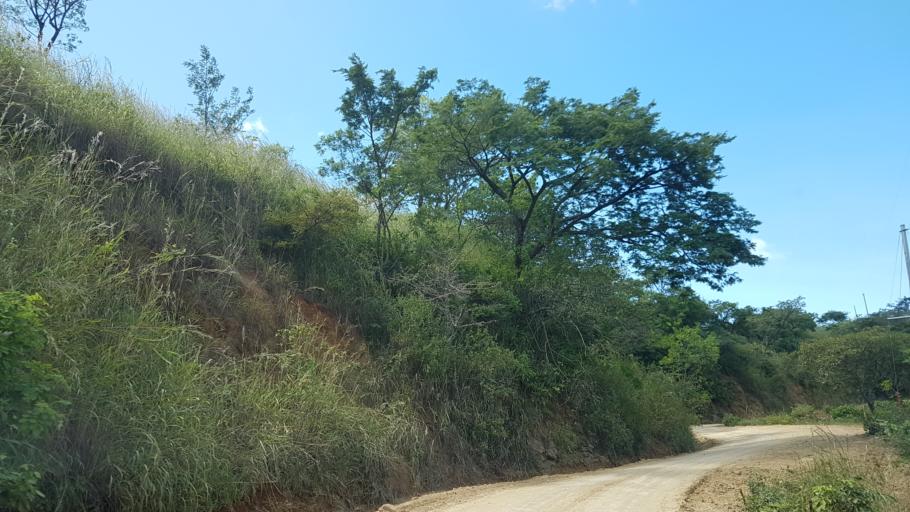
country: HN
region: El Paraiso
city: Oropoli
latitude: 13.7401
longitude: -86.7024
